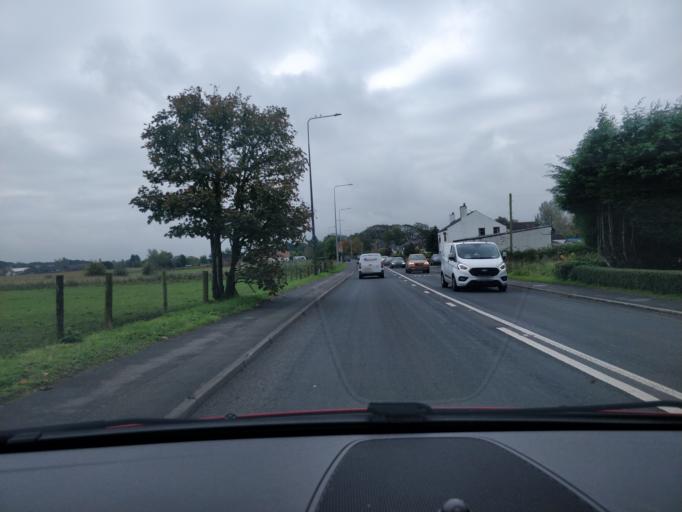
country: GB
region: England
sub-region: Lancashire
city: Banks
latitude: 53.6167
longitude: -2.9399
